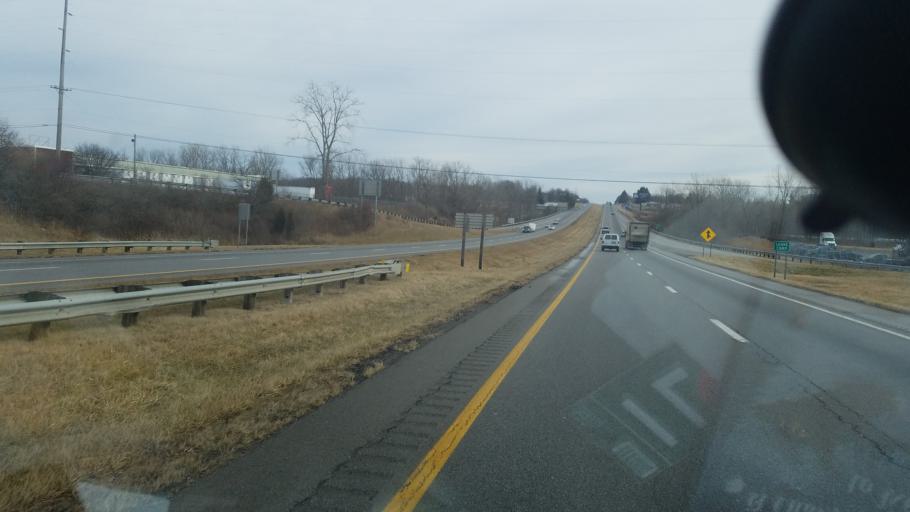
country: US
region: Ohio
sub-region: Richland County
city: Lincoln Heights
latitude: 40.7790
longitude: -82.4947
